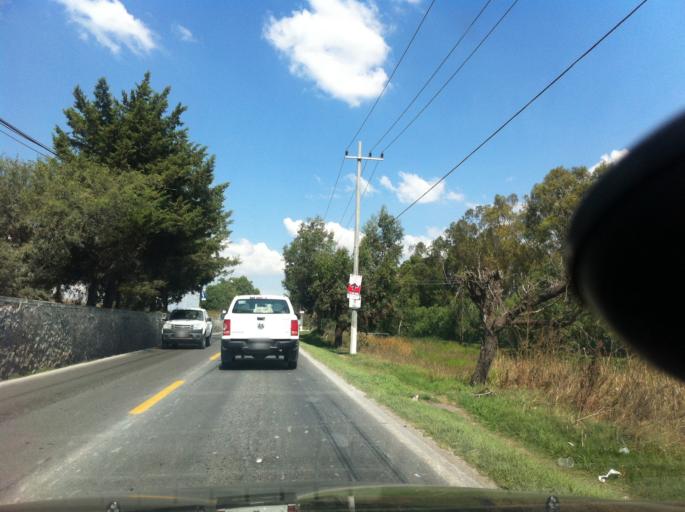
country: MX
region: Mexico
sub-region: Cuautitlan
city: La Providencia
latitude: 19.7589
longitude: -99.1270
